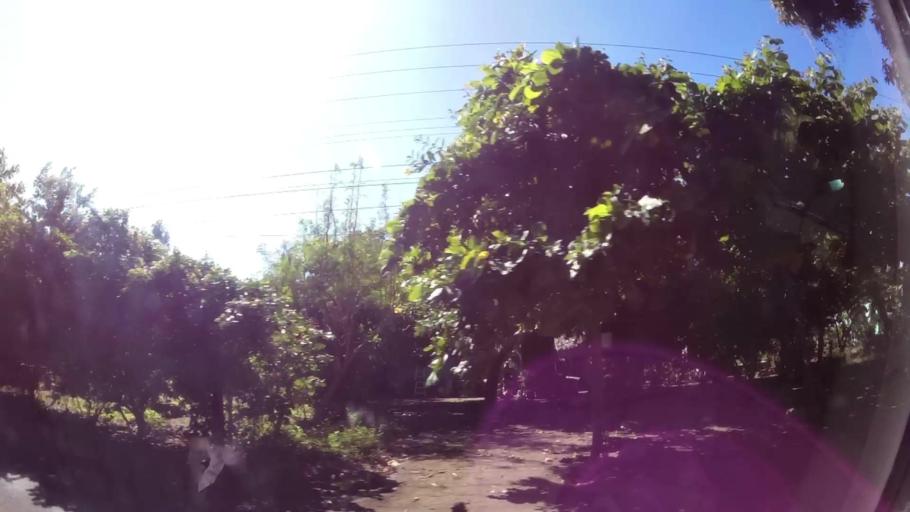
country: GT
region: Escuintla
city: Iztapa
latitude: 13.9227
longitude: -90.5742
